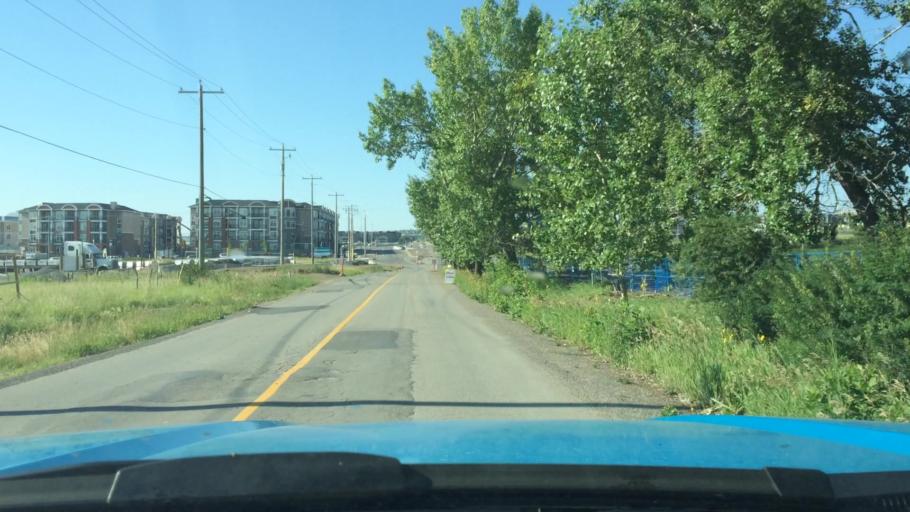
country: CA
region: Alberta
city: Calgary
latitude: 51.1742
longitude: -114.1412
